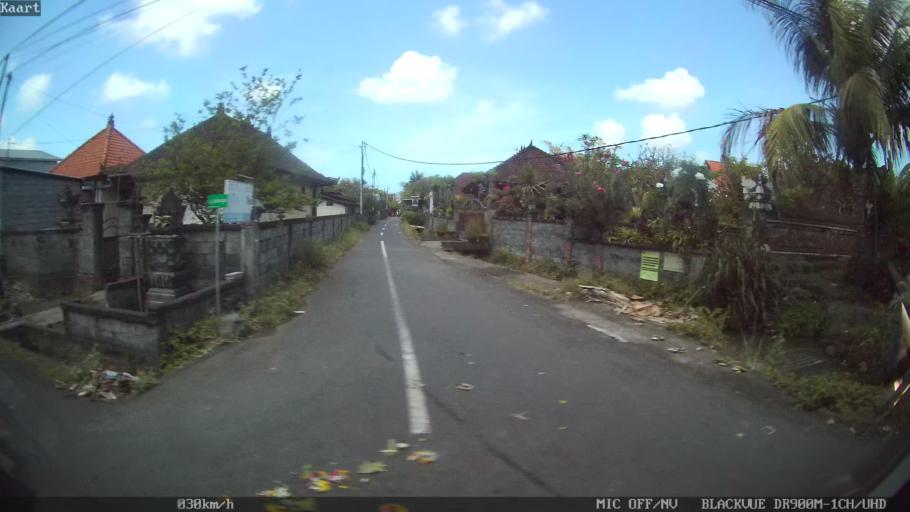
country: ID
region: Bali
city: Banjar Jabejero
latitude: -8.5925
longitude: 115.2600
